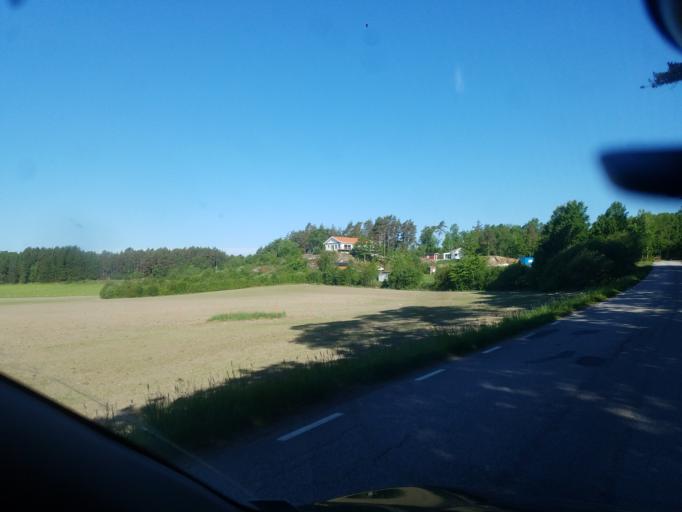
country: SE
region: Vaestra Goetaland
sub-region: Orust
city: Henan
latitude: 58.2831
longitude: 11.5840
